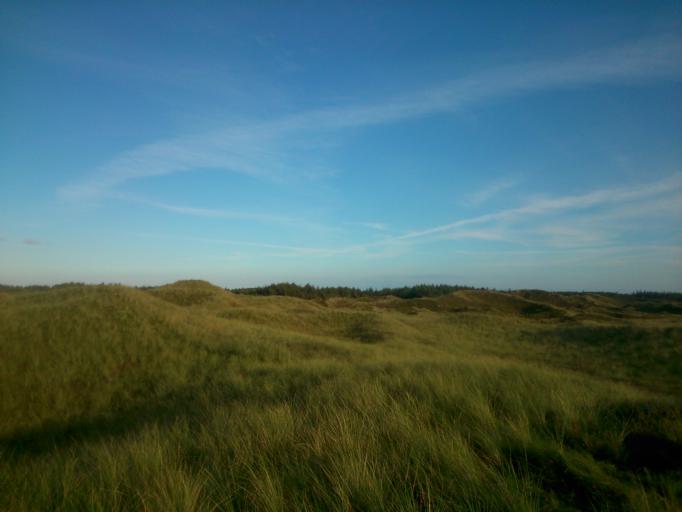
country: DK
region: South Denmark
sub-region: Varde Kommune
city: Oksbol
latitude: 55.6939
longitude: 8.1557
